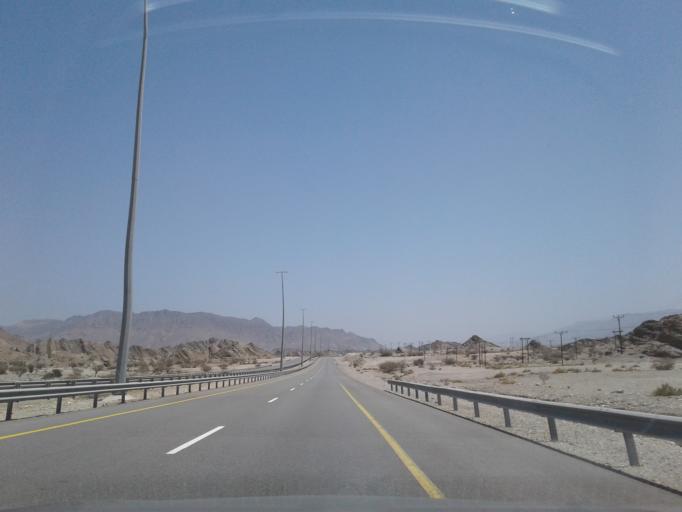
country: OM
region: Muhafazat Masqat
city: Muscat
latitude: 23.3488
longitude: 58.6911
